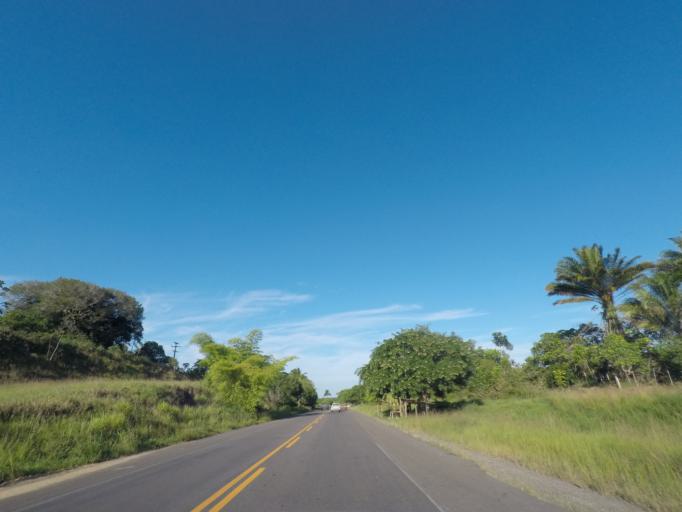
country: BR
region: Bahia
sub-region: Nazare
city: Nazare
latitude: -13.0096
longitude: -38.9713
